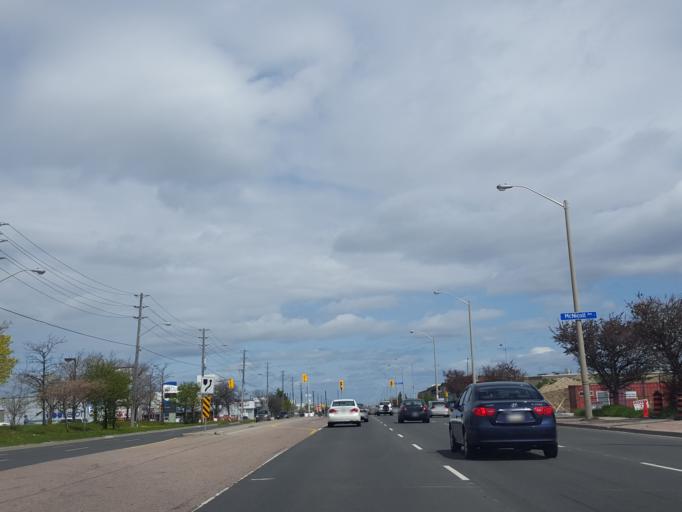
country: CA
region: Ontario
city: Markham
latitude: 43.8228
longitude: -79.2471
